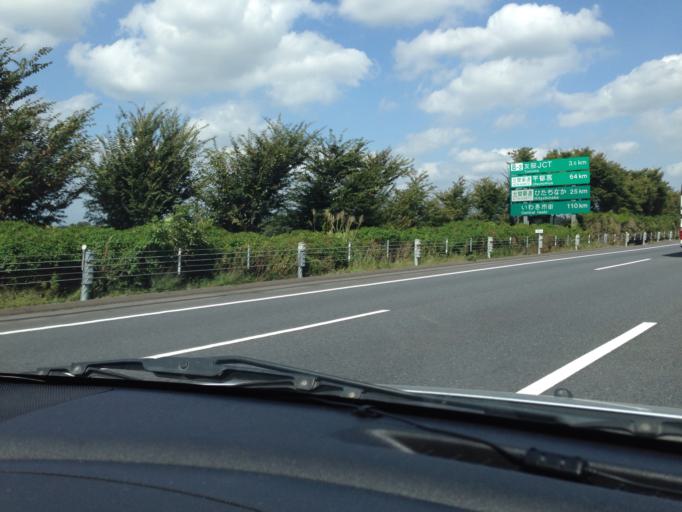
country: JP
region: Ibaraki
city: Tomobe
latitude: 36.2902
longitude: 140.3295
